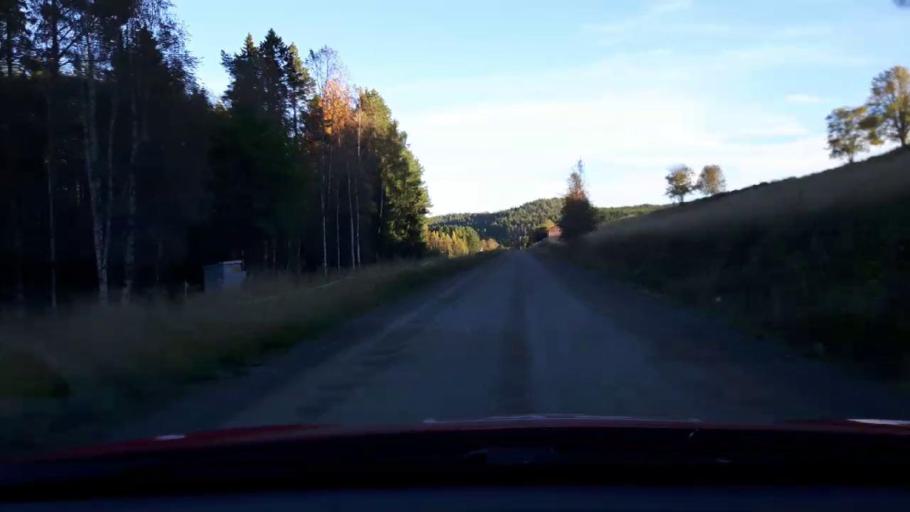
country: SE
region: Jaemtland
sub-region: OEstersunds Kommun
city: Brunflo
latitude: 62.9234
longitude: 15.0099
